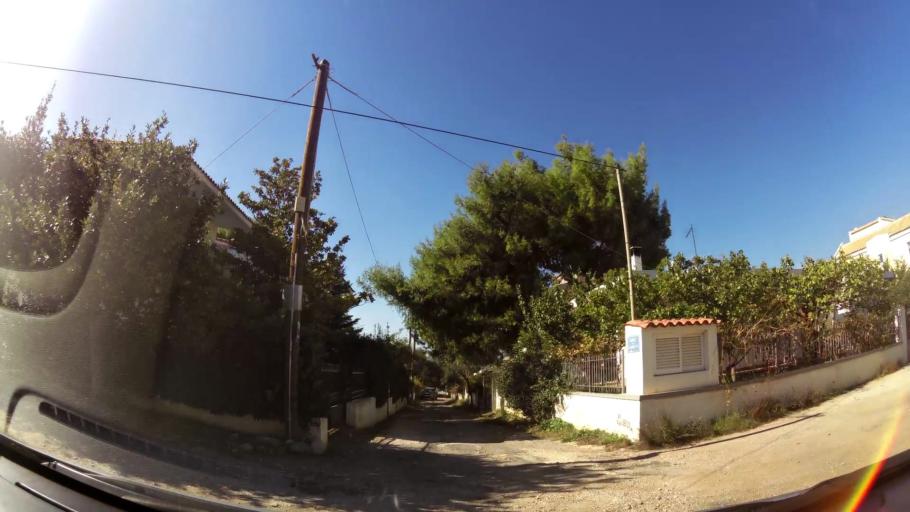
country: GR
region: Attica
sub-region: Nomarchia Athinas
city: Nea Erythraia
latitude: 38.1017
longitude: 23.8241
